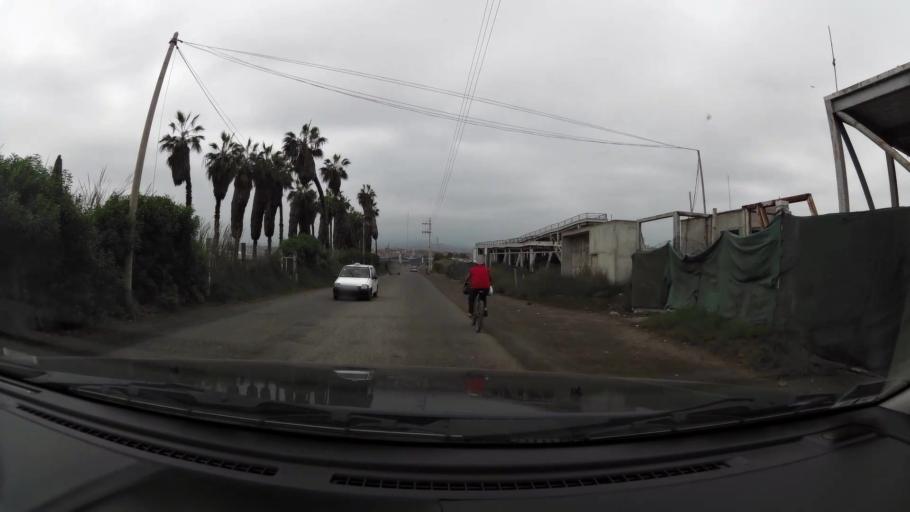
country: PE
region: Lima
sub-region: Lima
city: Surco
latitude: -12.2108
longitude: -76.9891
